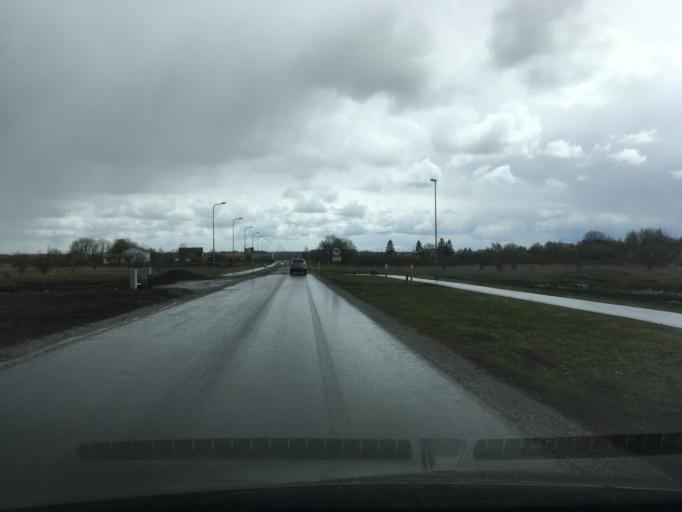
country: EE
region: Harju
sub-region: Joelaehtme vald
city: Loo
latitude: 59.4462
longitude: 24.9574
